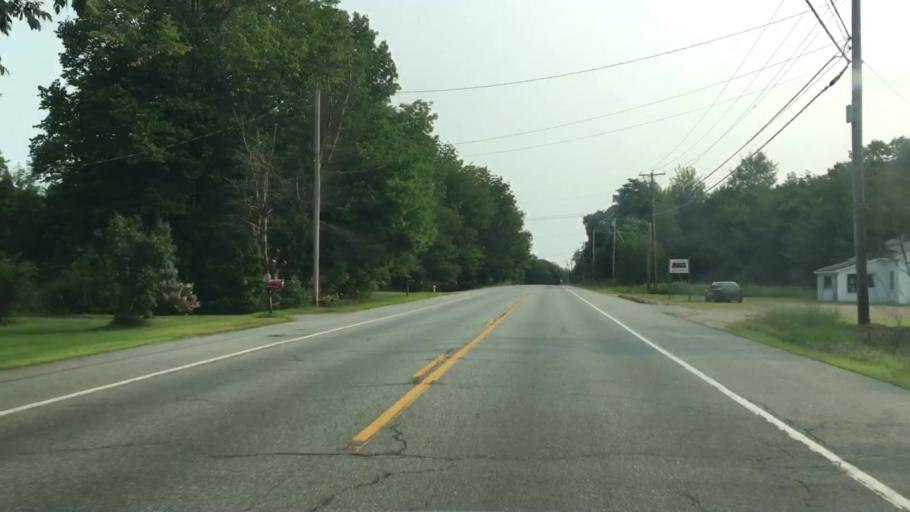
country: US
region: Maine
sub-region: Kennebec County
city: Gardiner
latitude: 44.1921
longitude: -69.8117
